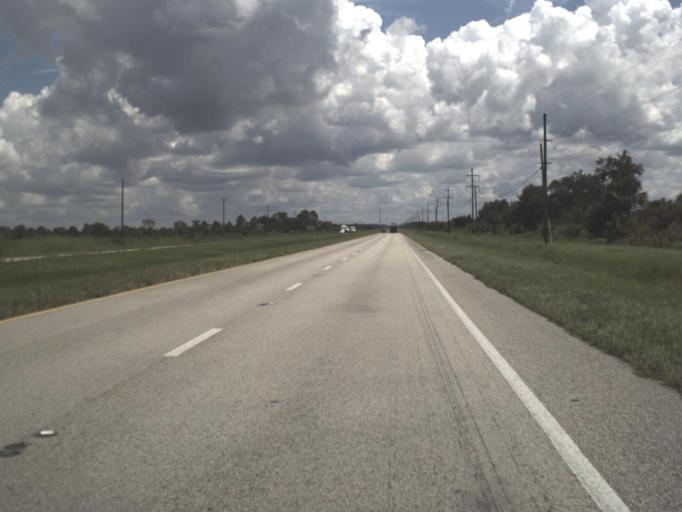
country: US
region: Florida
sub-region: Polk County
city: Babson Park
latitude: 27.8434
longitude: -81.3580
